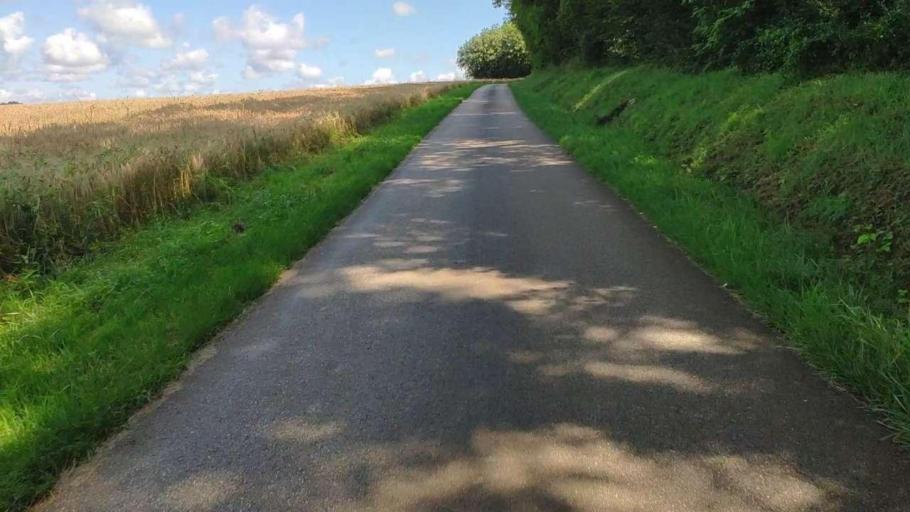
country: FR
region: Franche-Comte
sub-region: Departement du Jura
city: Bletterans
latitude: 46.8026
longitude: 5.5526
